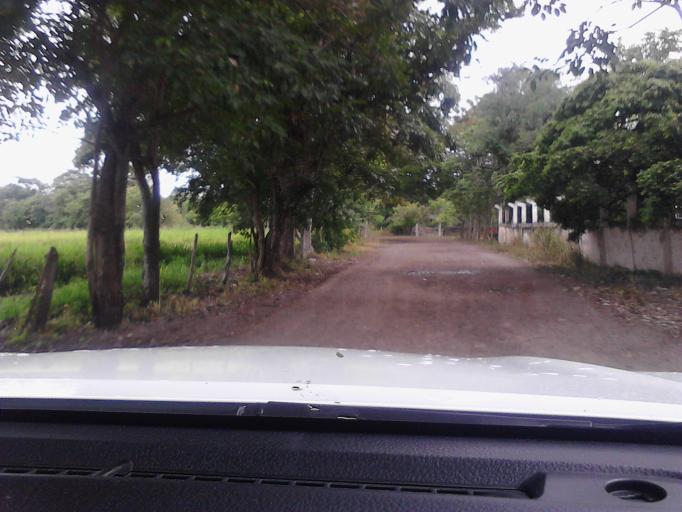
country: NI
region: Matagalpa
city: Ciudad Dario
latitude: 12.9004
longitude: -86.1406
